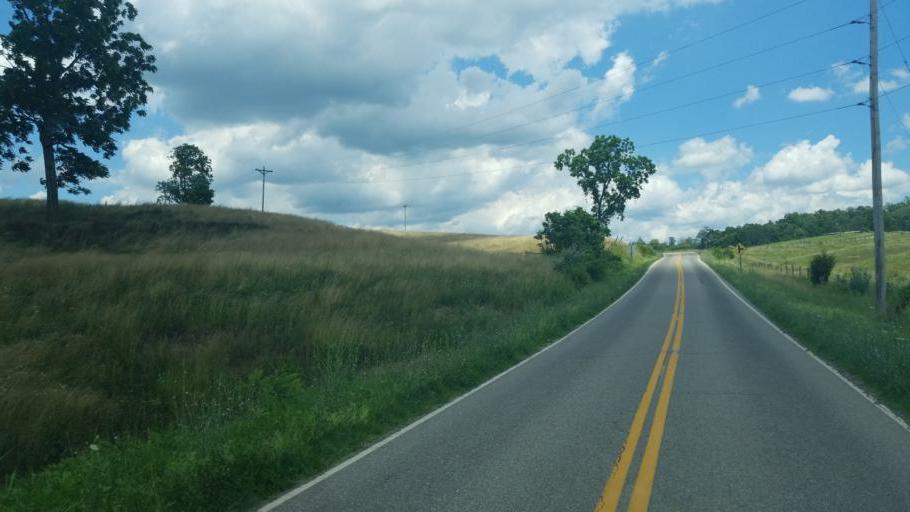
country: US
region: Ohio
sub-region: Gallia County
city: Gallipolis
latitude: 38.7535
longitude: -82.3604
